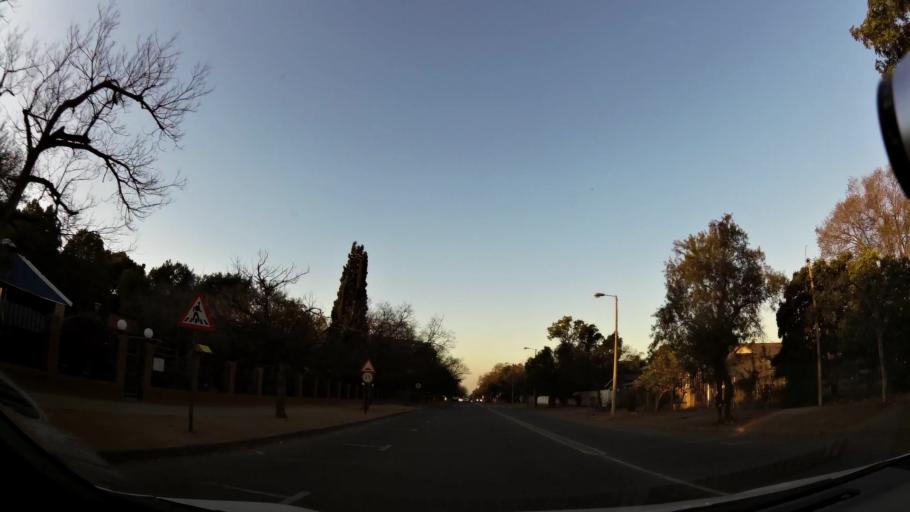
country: ZA
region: North-West
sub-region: Bojanala Platinum District Municipality
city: Rustenburg
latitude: -25.6740
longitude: 27.2248
